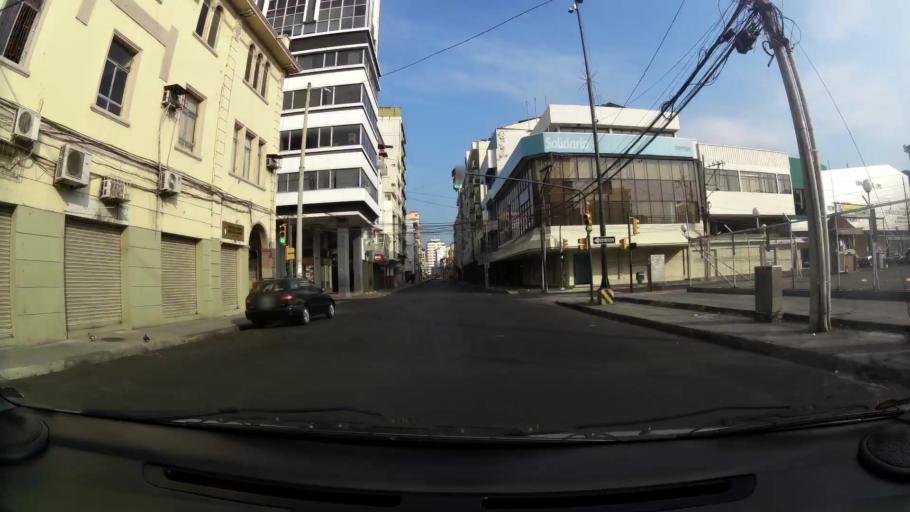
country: EC
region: Guayas
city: Eloy Alfaro
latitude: -2.1898
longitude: -79.8809
